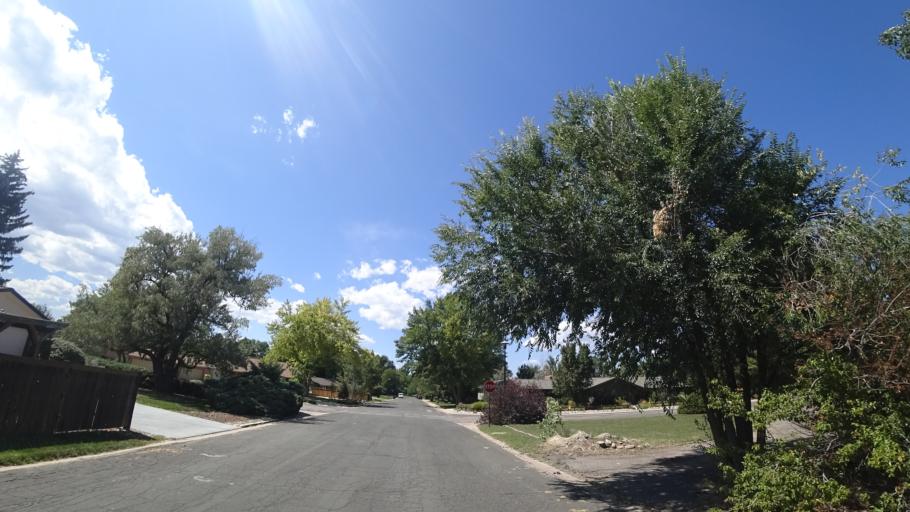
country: US
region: Colorado
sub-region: Arapahoe County
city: Littleton
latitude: 39.6091
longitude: -104.9941
